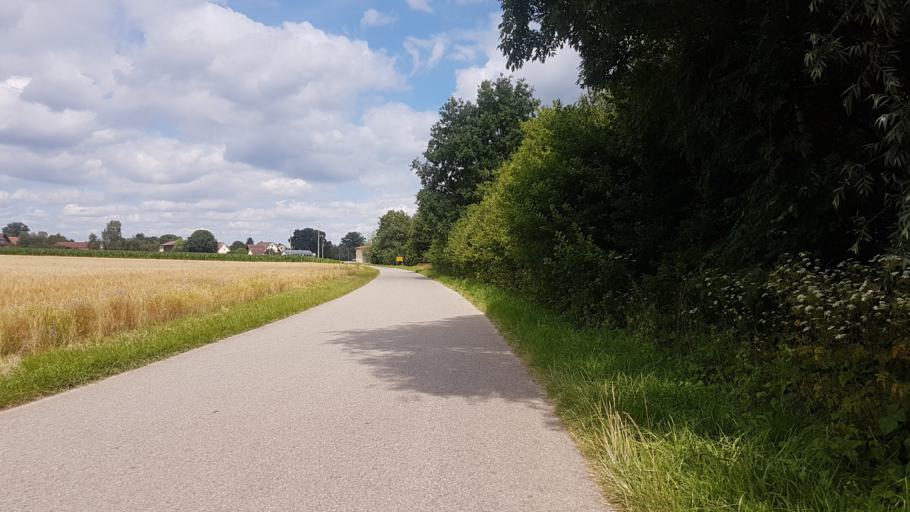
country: DE
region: Bavaria
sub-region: Regierungsbezirk Mittelfranken
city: Gunzenhausen
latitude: 49.0924
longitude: 10.7593
